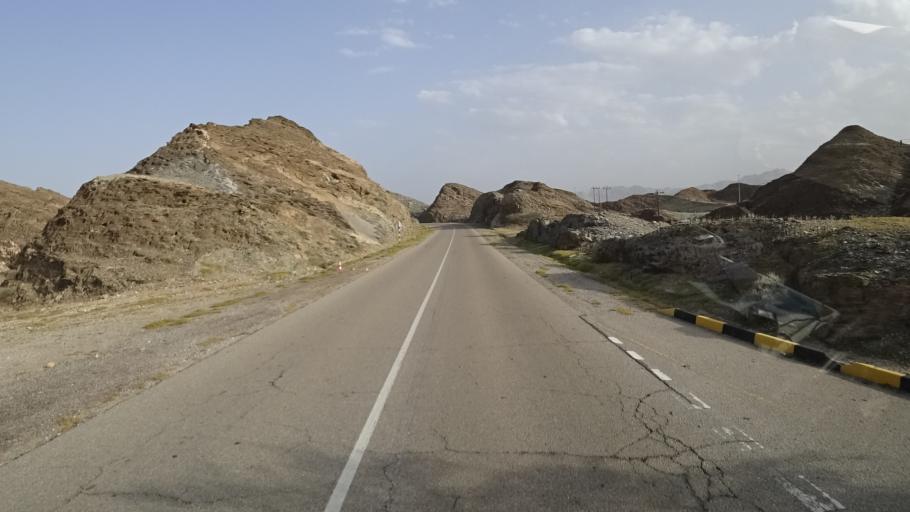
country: OM
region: Muhafazat Masqat
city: Bawshar
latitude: 23.3610
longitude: 58.5254
